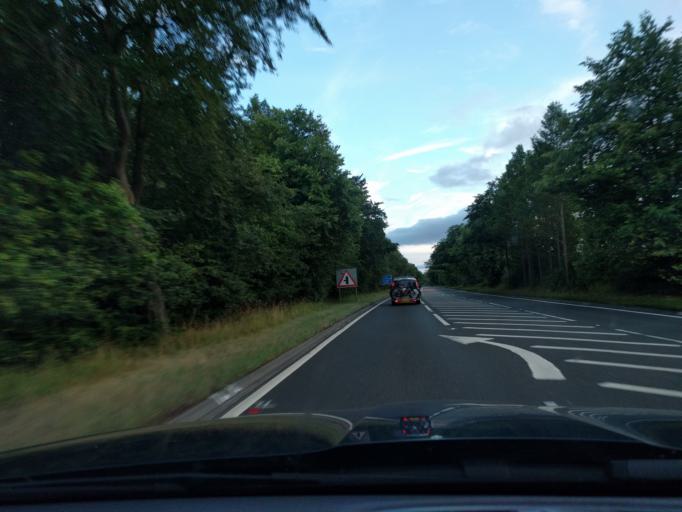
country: GB
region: England
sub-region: Northumberland
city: Hebron
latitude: 55.2214
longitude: -1.7075
